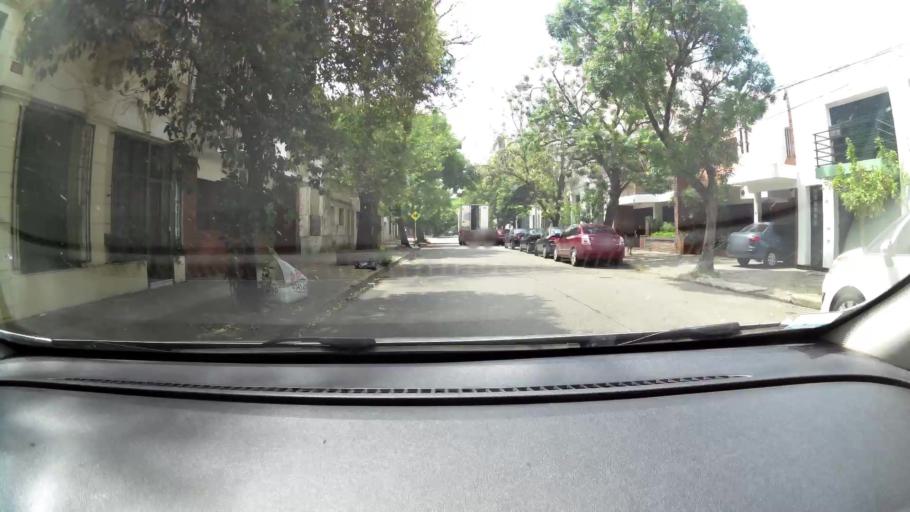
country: AR
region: Santa Fe
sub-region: Departamento de Rosario
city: Rosario
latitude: -32.9607
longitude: -60.6352
